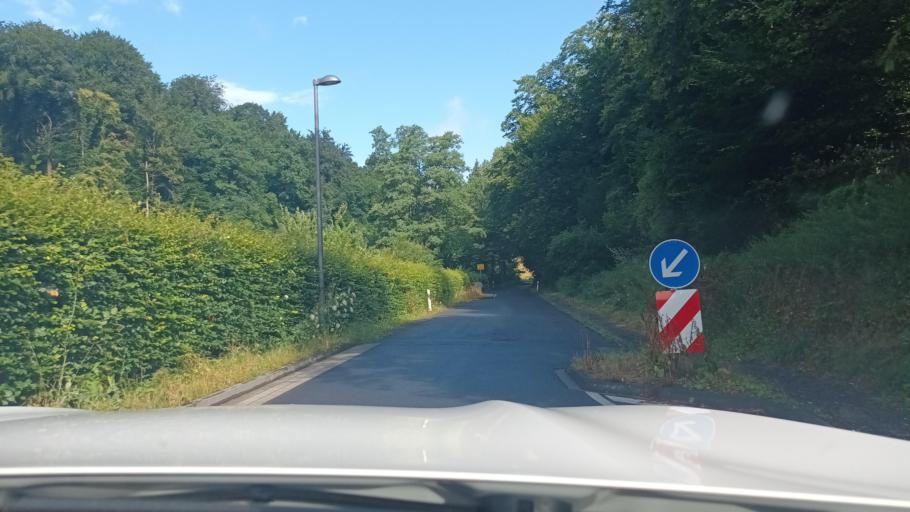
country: DE
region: North Rhine-Westphalia
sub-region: Regierungsbezirk Koln
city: Hennef
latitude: 50.7933
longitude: 7.3230
